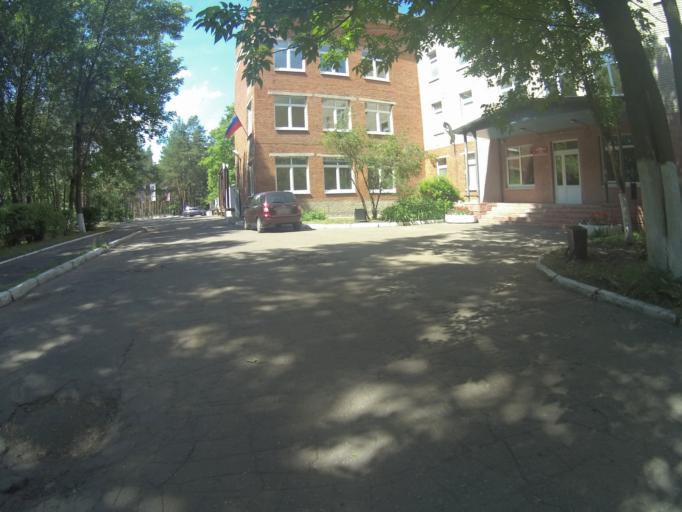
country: RU
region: Vladimir
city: Kommunar
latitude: 56.1009
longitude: 40.4415
